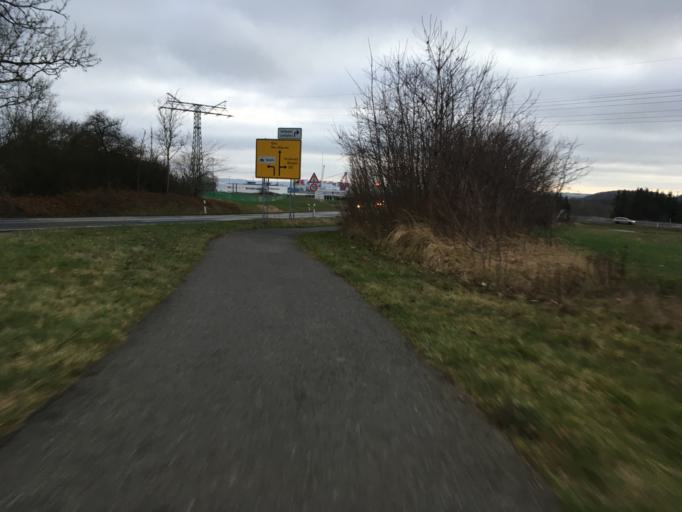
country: DE
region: Mecklenburg-Vorpommern
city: Sagard
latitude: 54.4941
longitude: 13.5782
